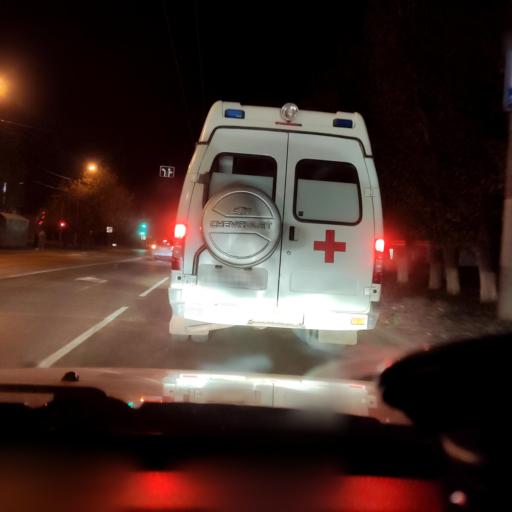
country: RU
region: Perm
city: Perm
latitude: 57.9694
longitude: 56.2454
